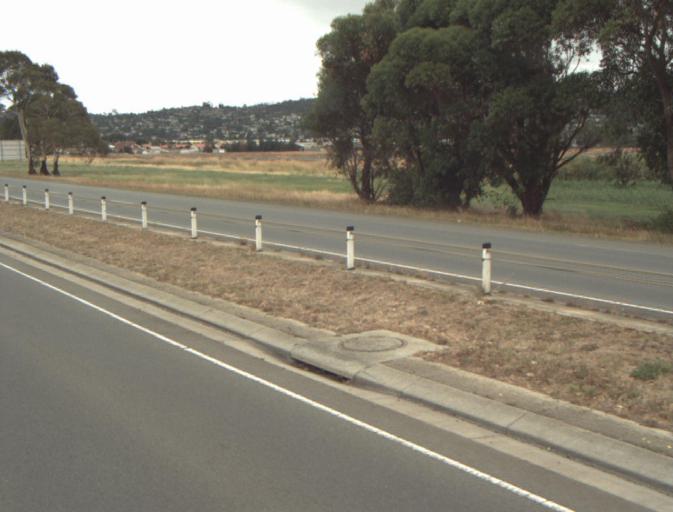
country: AU
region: Tasmania
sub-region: Launceston
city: Newnham
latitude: -41.4150
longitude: 147.1300
